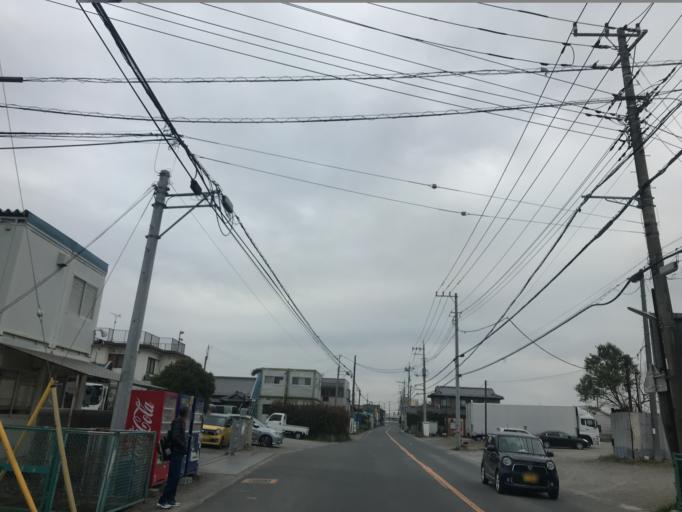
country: JP
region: Saitama
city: Yashio-shi
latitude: 35.8369
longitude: 139.8411
